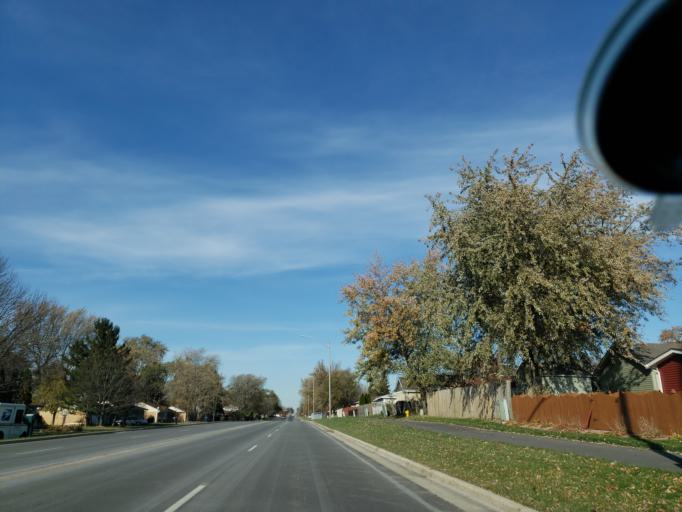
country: US
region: Illinois
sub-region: Cook County
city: Tinley Park
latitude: 41.5910
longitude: -87.7848
